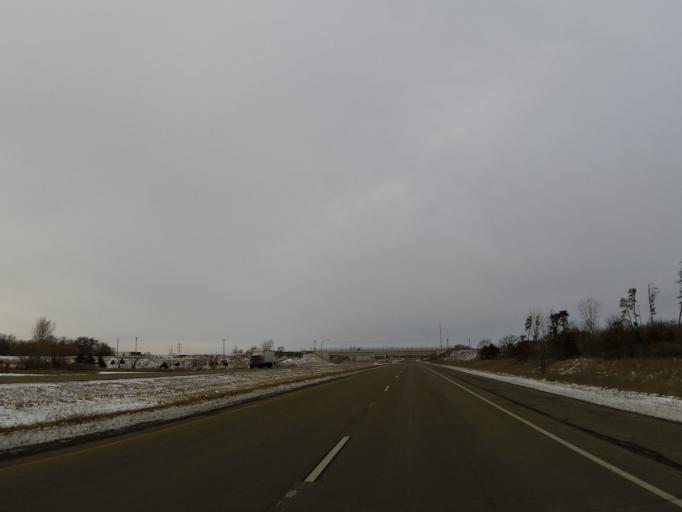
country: US
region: Minnesota
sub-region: Scott County
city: Savage
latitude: 44.7847
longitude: -93.4049
